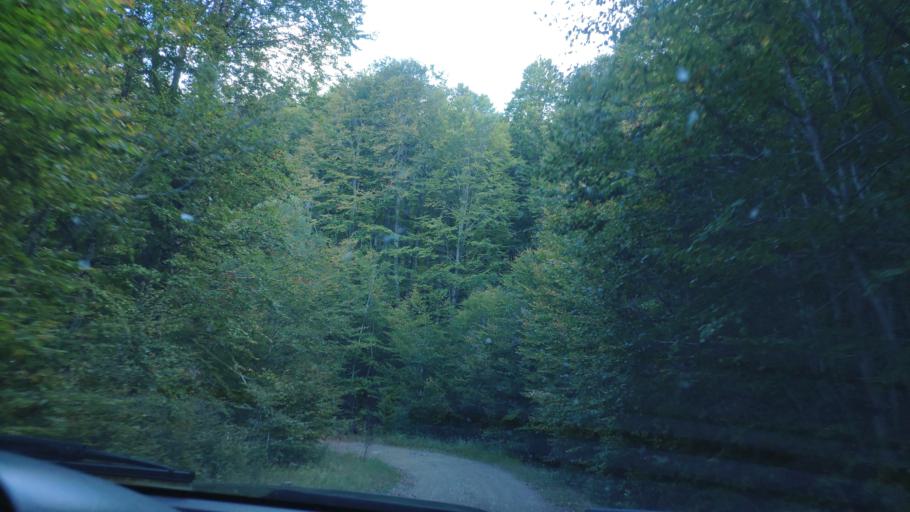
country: GR
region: West Macedonia
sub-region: Nomos Kastorias
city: Nestorio
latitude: 40.3262
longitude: 20.9015
